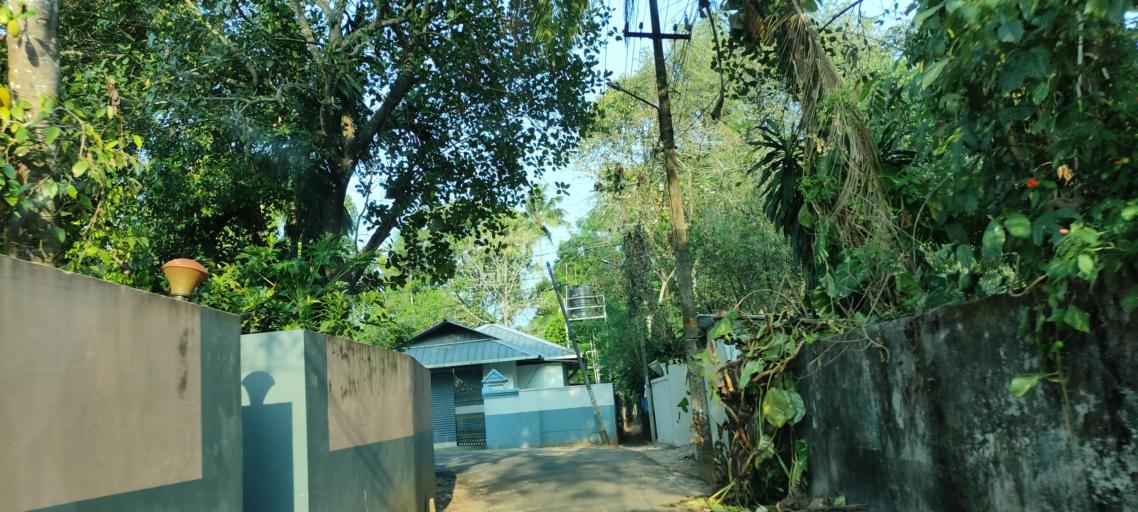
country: IN
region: Kerala
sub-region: Alappuzha
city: Alleppey
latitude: 9.5121
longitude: 76.3223
